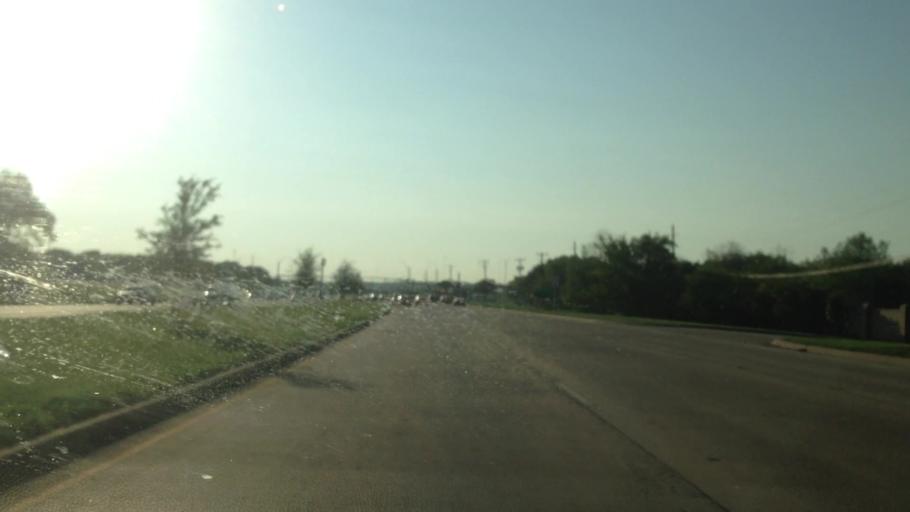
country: US
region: Texas
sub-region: Tarrant County
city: Pantego
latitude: 32.7213
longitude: -97.1786
